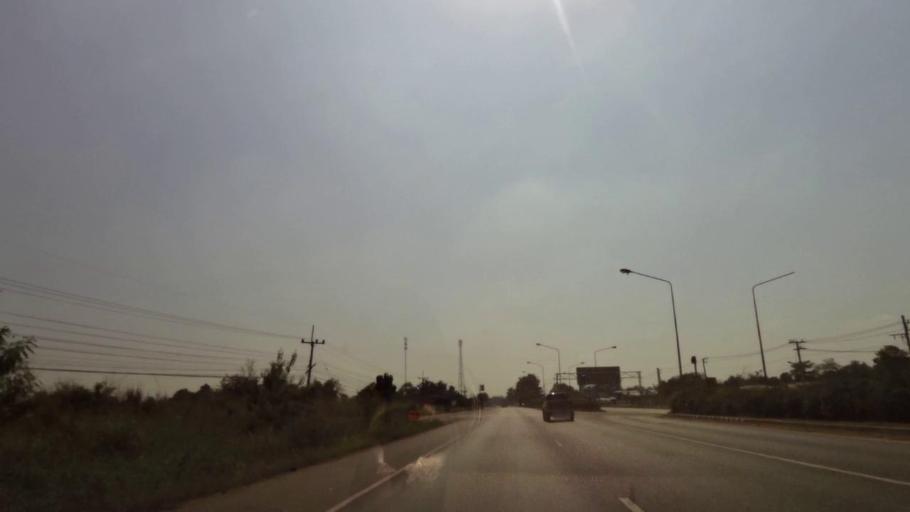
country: TH
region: Phichit
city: Wachira Barami
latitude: 16.3495
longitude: 100.1285
